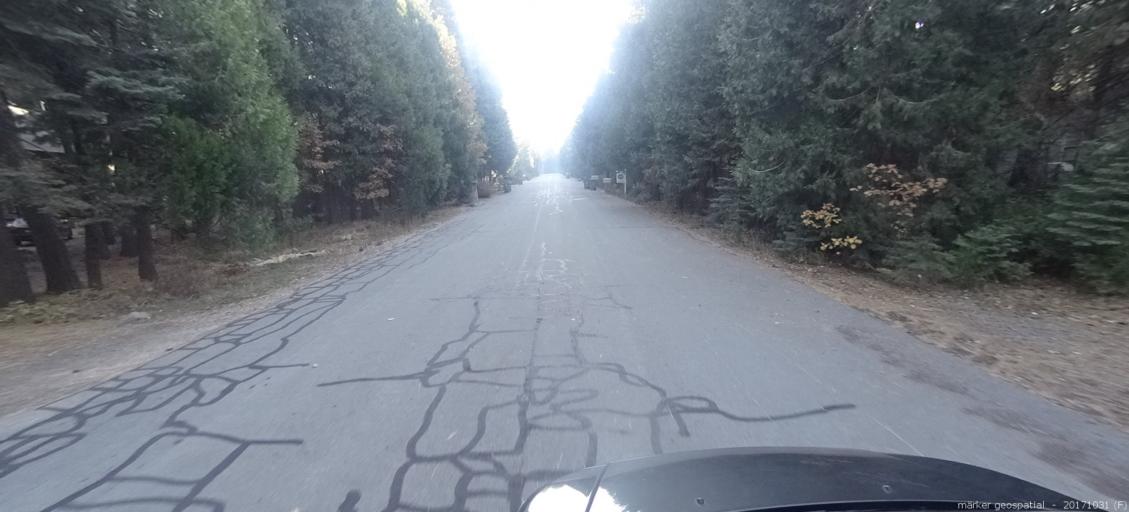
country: US
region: California
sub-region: Shasta County
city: Shingletown
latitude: 40.5248
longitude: -121.7999
